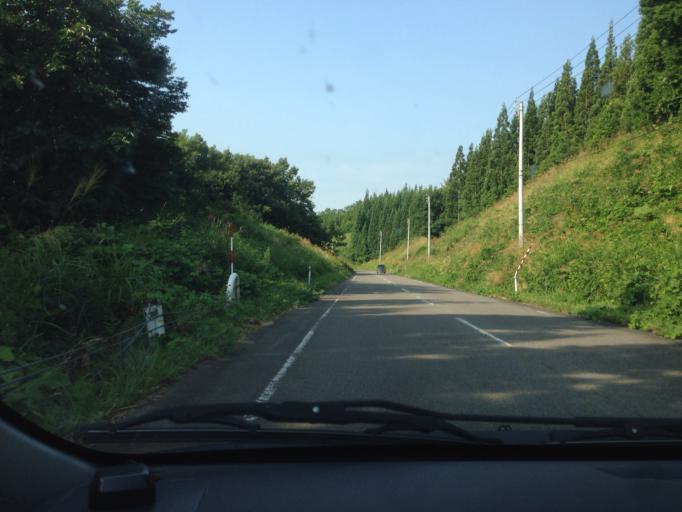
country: JP
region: Fukushima
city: Kitakata
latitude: 37.7453
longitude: 139.8703
